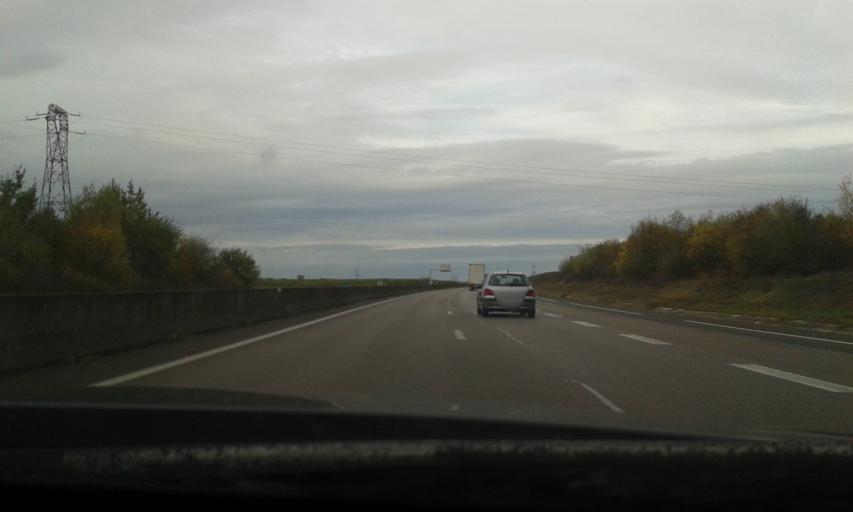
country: FR
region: Haute-Normandie
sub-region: Departement de l'Eure
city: La Madeleine-de-Nonancourt
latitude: 48.8352
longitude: 1.1832
